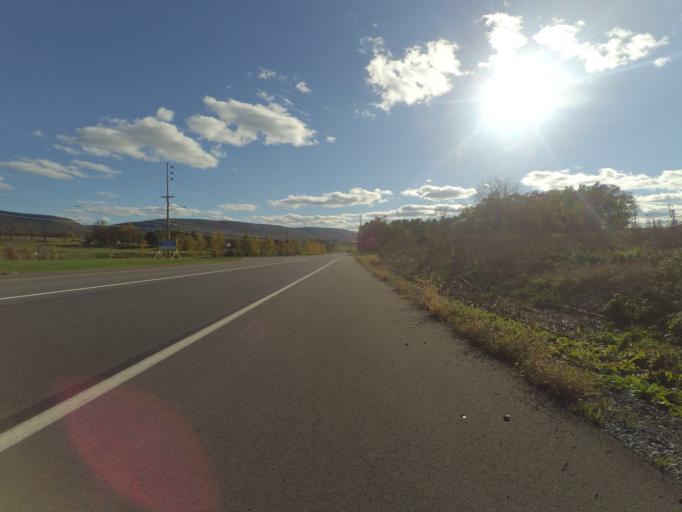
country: US
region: Pennsylvania
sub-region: Centre County
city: Pleasant Gap
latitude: 40.8677
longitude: -77.7803
